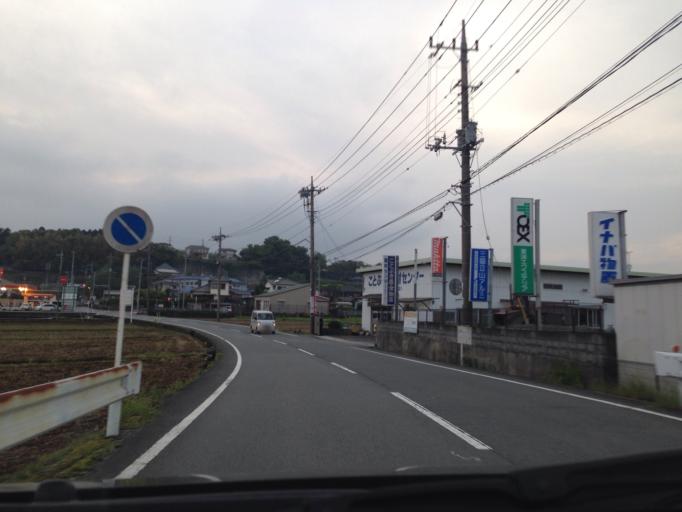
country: JP
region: Shizuoka
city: Mishima
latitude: 35.1696
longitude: 138.9210
